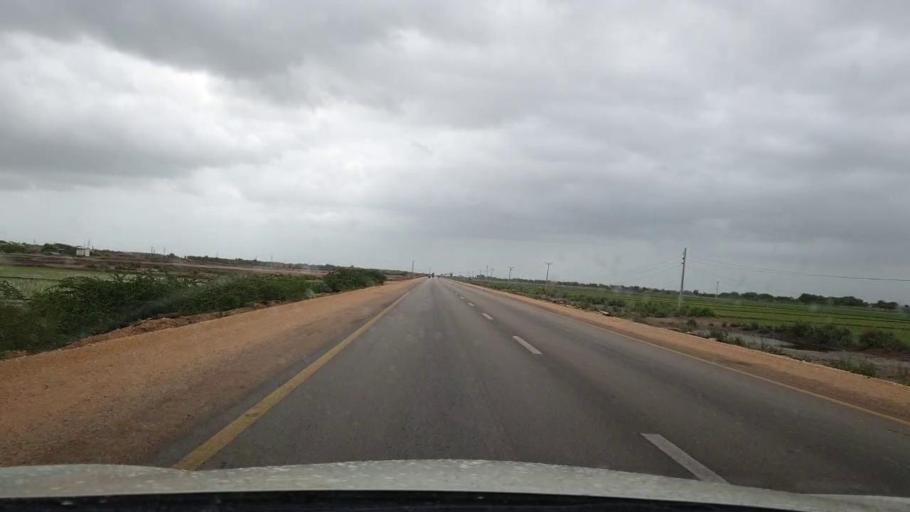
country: PK
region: Sindh
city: Badin
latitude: 24.6560
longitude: 68.7067
